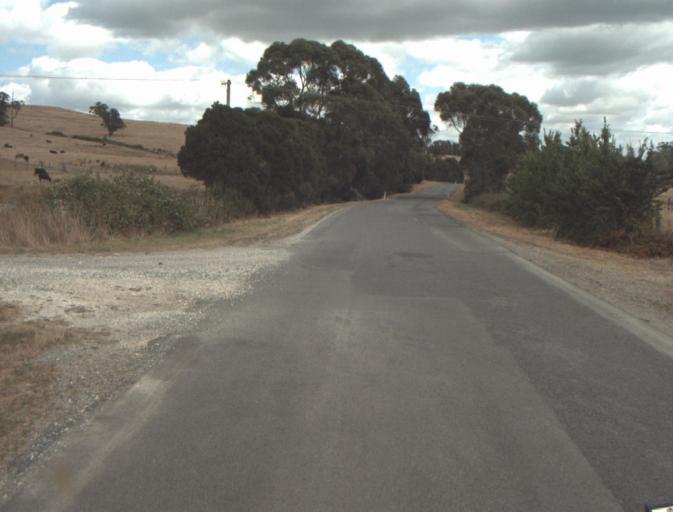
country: AU
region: Tasmania
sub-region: Launceston
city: Mayfield
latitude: -41.2036
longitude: 147.0789
